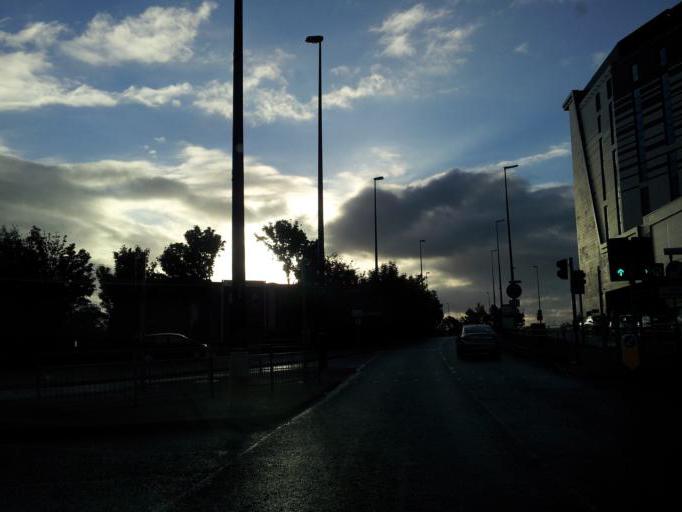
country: GB
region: England
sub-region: Trafford
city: Trafford Park
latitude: 53.4649
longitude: -2.2895
